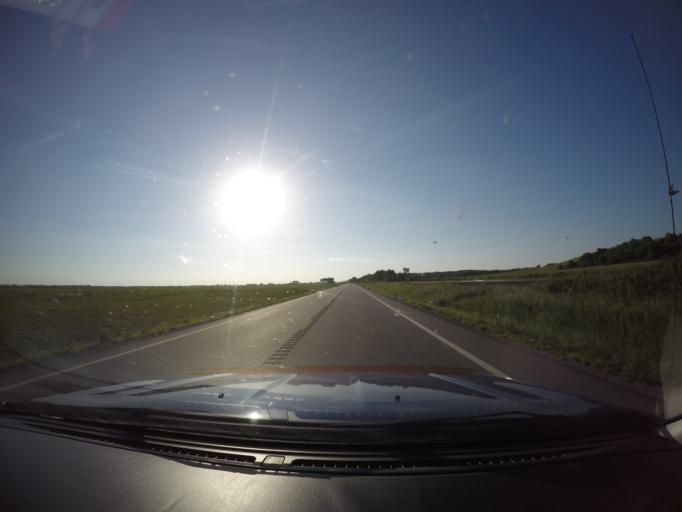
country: US
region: Kansas
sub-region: Pottawatomie County
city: Saint Marys
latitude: 39.1700
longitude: -96.0160
